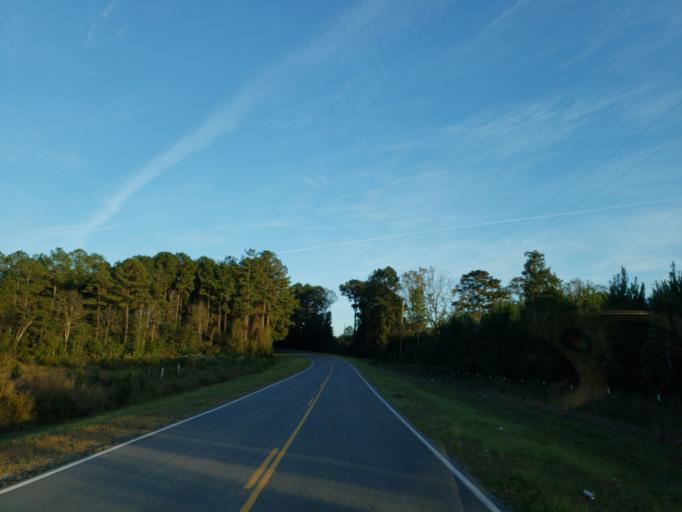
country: US
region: Mississippi
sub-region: Wayne County
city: Belmont
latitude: 31.4420
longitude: -88.5103
